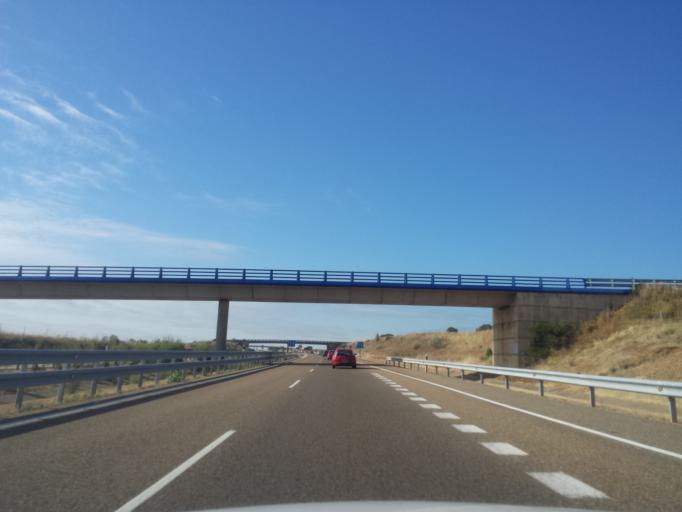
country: ES
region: Castille and Leon
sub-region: Provincia de Leon
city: Valdevimbre
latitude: 42.3945
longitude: -5.5960
